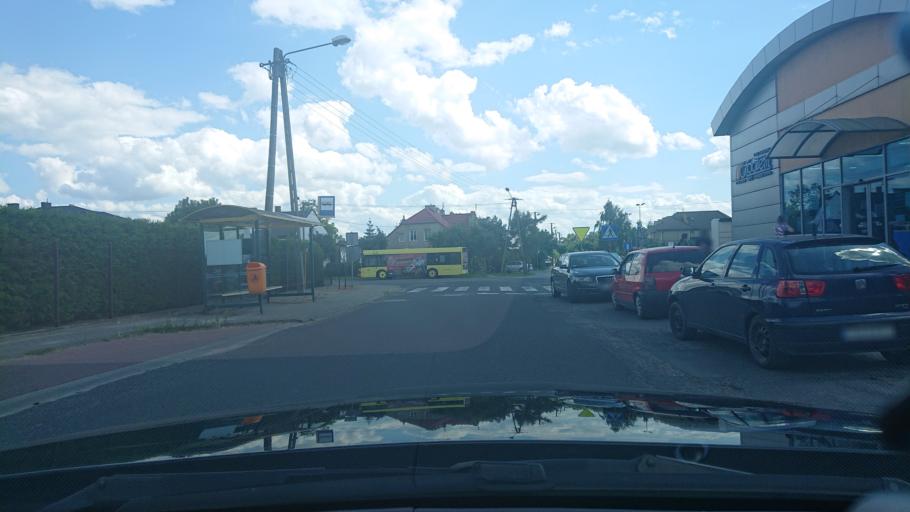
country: PL
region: Greater Poland Voivodeship
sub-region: Powiat gnieznienski
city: Gniezno
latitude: 52.5340
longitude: 17.6359
